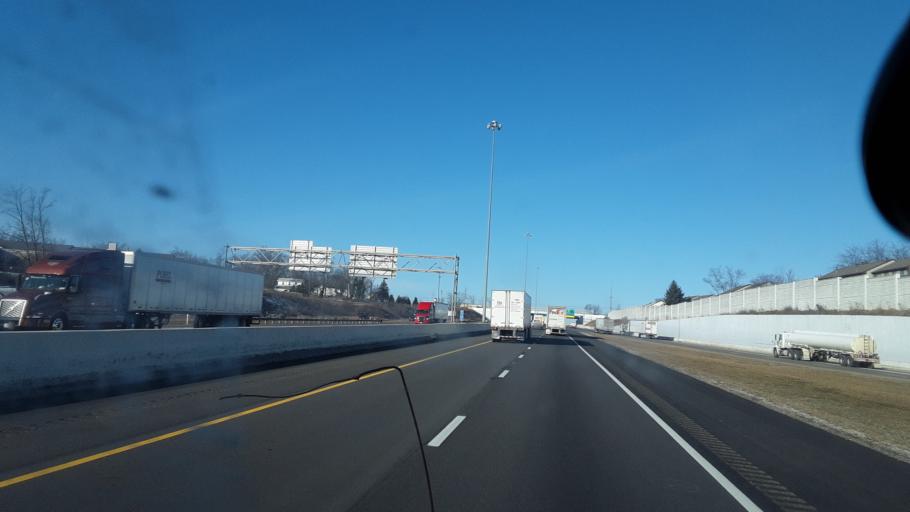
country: US
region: Ohio
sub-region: Montgomery County
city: Vandalia
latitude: 39.8656
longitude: -84.1932
